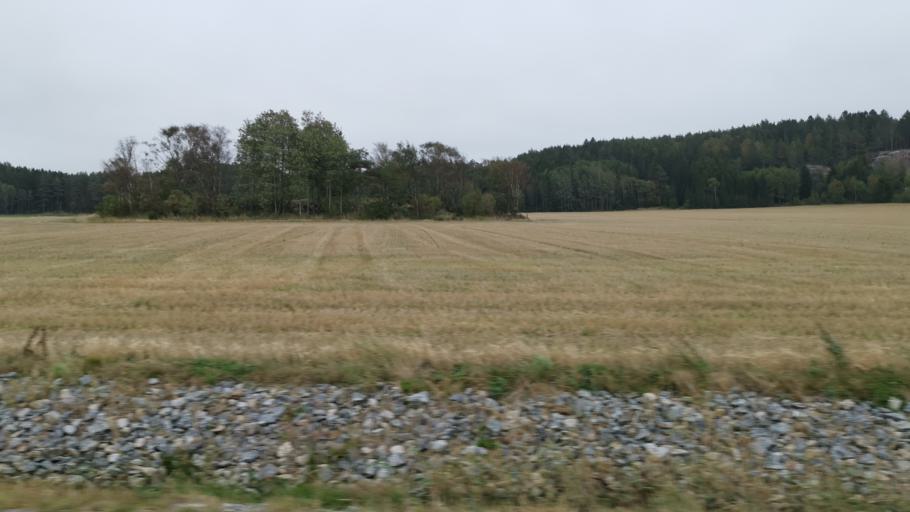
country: SE
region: Vaestra Goetaland
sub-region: Tanums Kommun
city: Tanumshede
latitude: 58.6679
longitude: 11.3432
